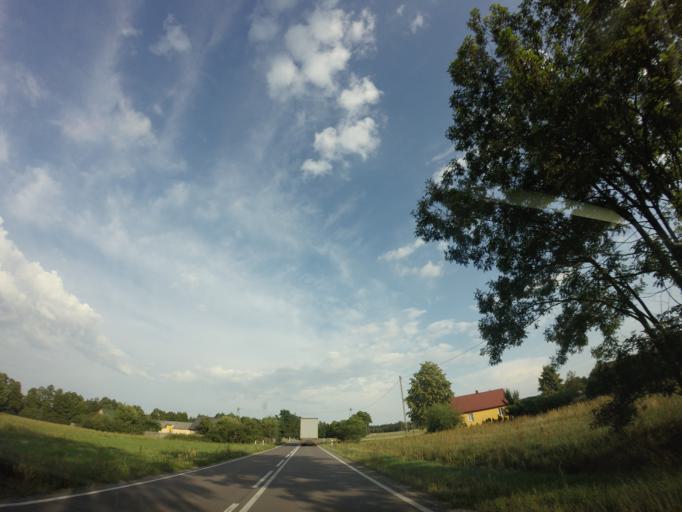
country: PL
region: Lublin Voivodeship
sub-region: Powiat lubartowski
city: Jeziorzany
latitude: 51.5747
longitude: 22.2893
